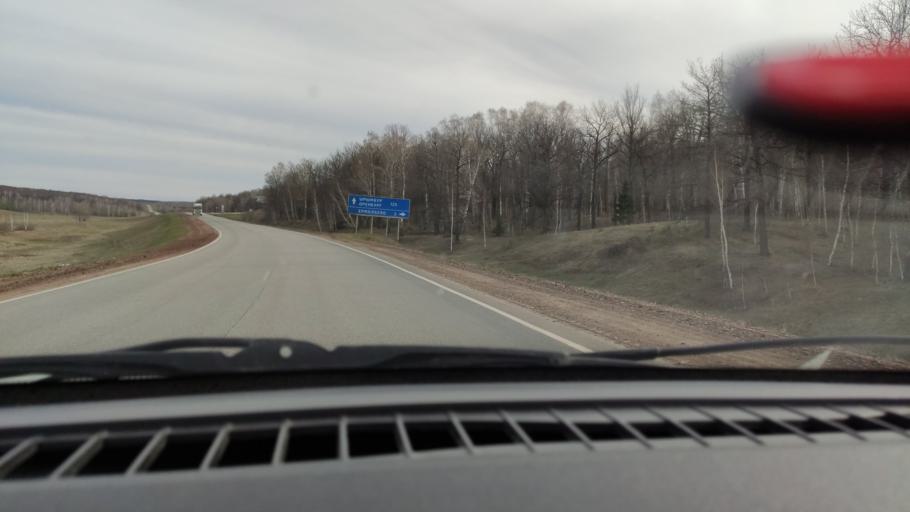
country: RU
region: Bashkortostan
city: Yermolayevo
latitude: 52.7006
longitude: 55.8538
